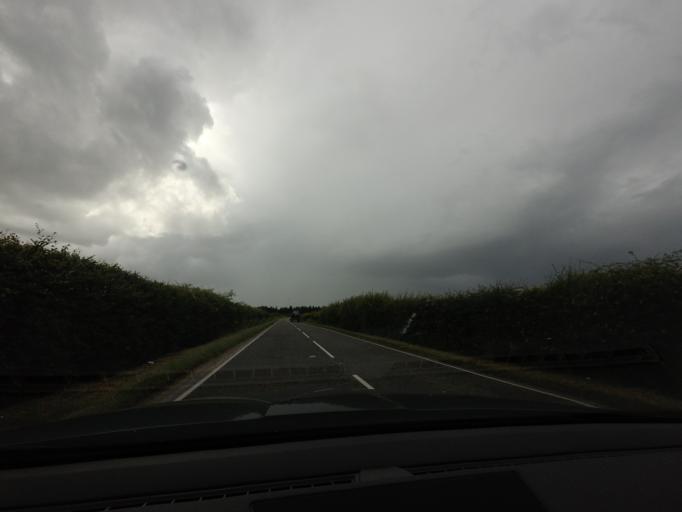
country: GB
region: Scotland
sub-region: Moray
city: Findochty
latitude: 57.6721
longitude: -2.9157
